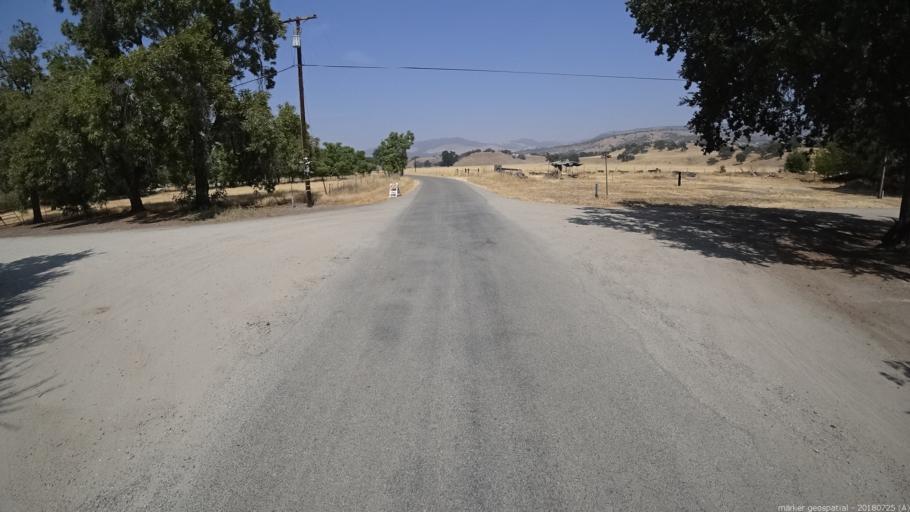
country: US
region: California
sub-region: Fresno County
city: Coalinga
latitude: 35.9008
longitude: -120.4328
